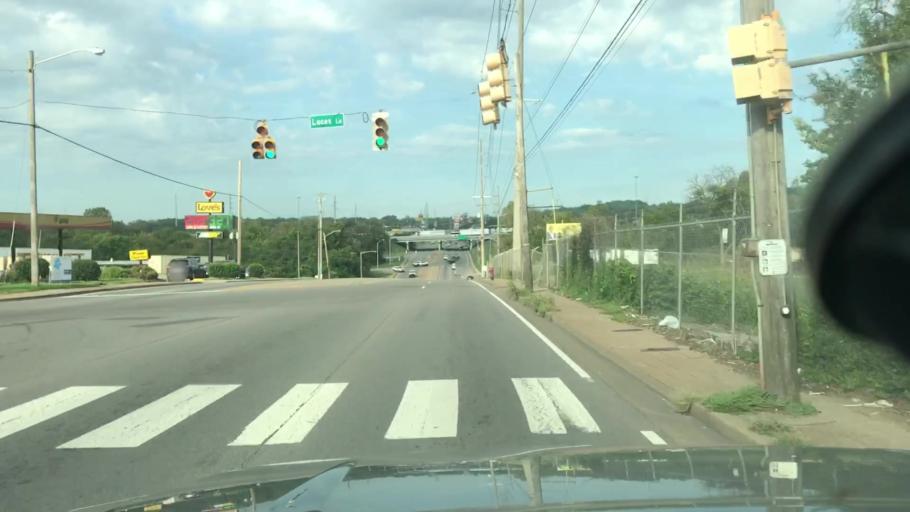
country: US
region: Tennessee
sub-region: Davidson County
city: Nashville
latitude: 36.2061
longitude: -86.7708
